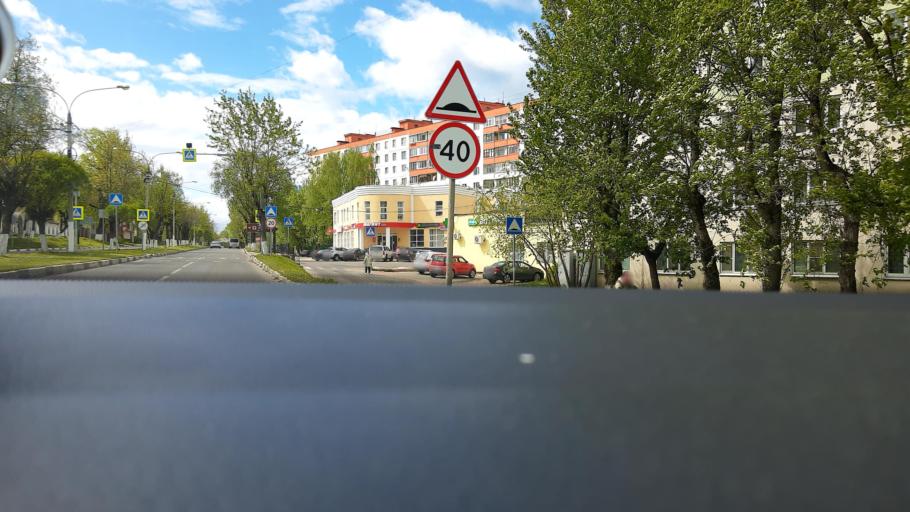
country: RU
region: Moskovskaya
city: Dmitrov
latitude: 56.3481
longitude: 37.5308
